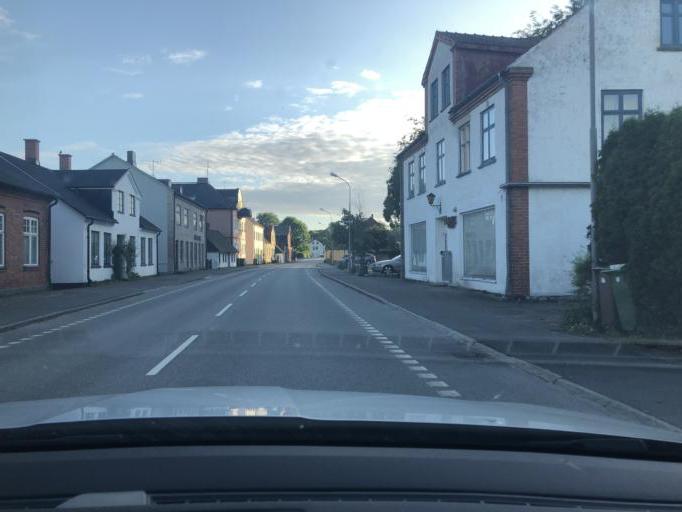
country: SE
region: Skane
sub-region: Simrishamns Kommun
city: Simrishamn
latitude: 55.4595
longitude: 14.1841
